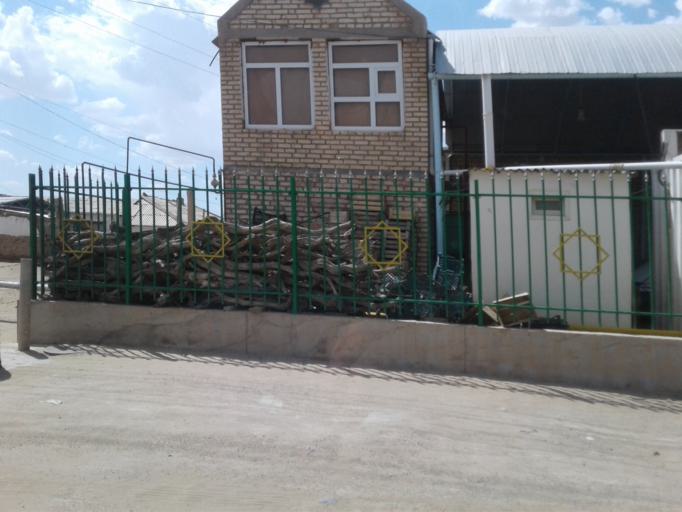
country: TM
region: Ahal
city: Abadan
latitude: 38.7634
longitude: 58.4921
